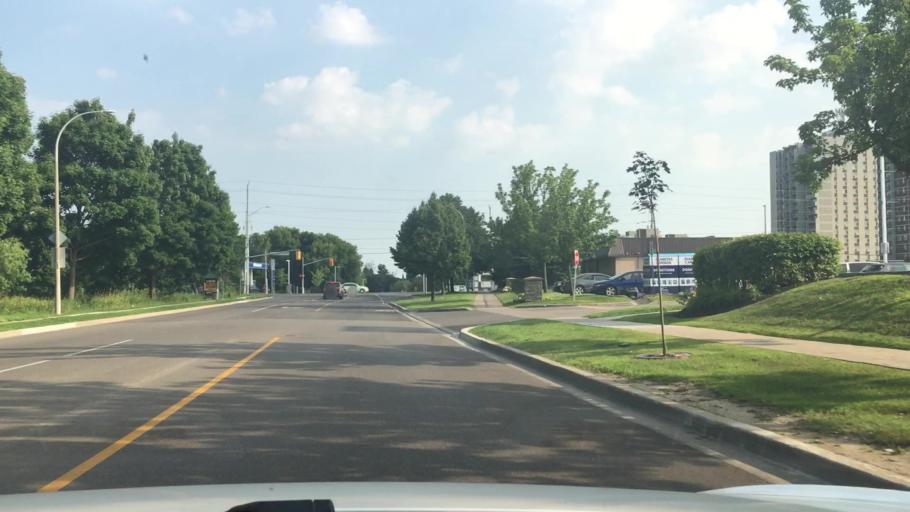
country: CA
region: Ontario
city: Ajax
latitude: 43.8766
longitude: -78.9622
